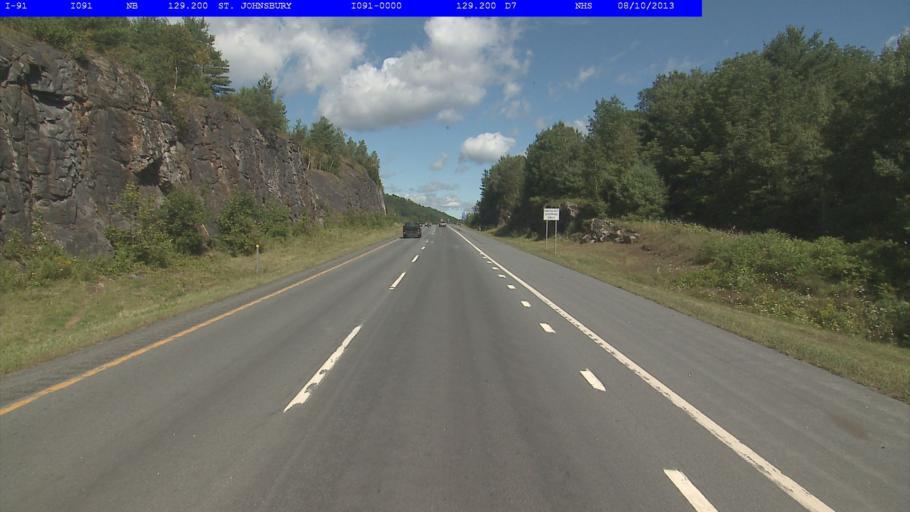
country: US
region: Vermont
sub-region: Caledonia County
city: Saint Johnsbury
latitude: 44.4089
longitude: -72.0255
